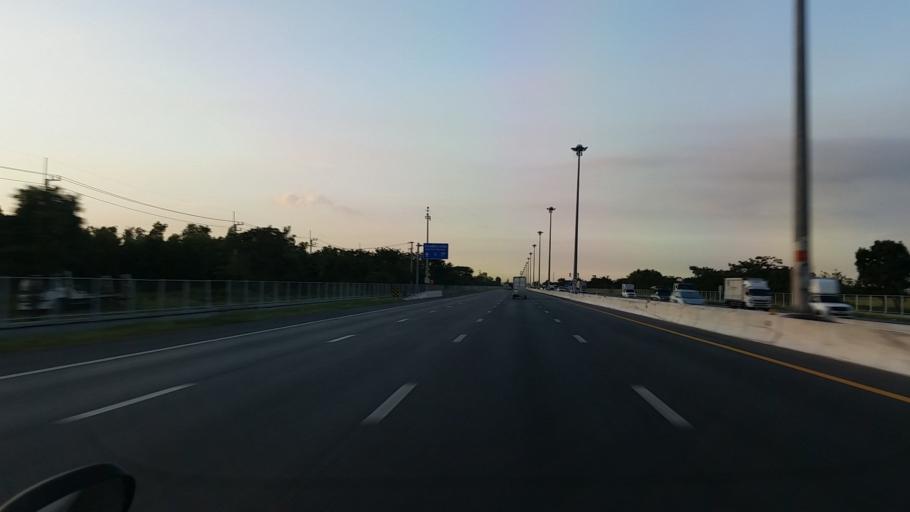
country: TH
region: Pathum Thani
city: Khlong Luang
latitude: 14.1488
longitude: 100.6595
